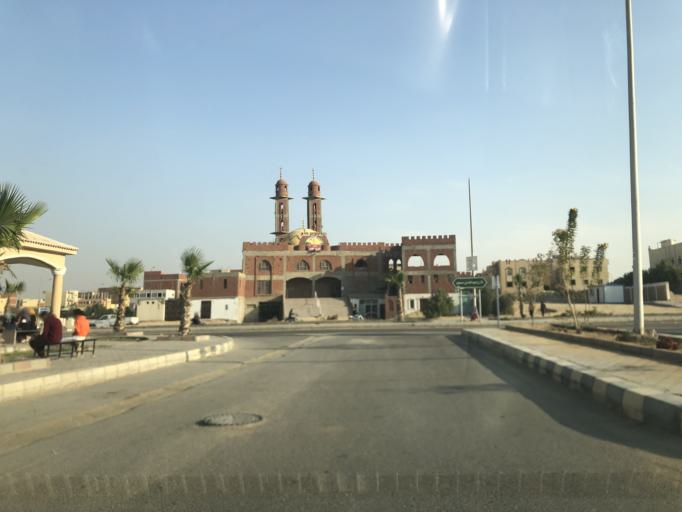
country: EG
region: Al Jizah
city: Madinat Sittah Uktubar
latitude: 29.9051
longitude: 30.9347
